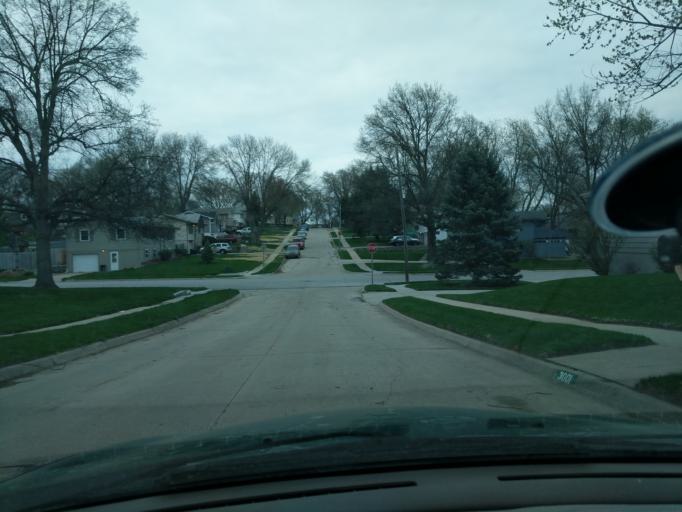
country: US
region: Nebraska
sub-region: Douglas County
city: Ralston
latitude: 41.2306
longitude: -96.0972
